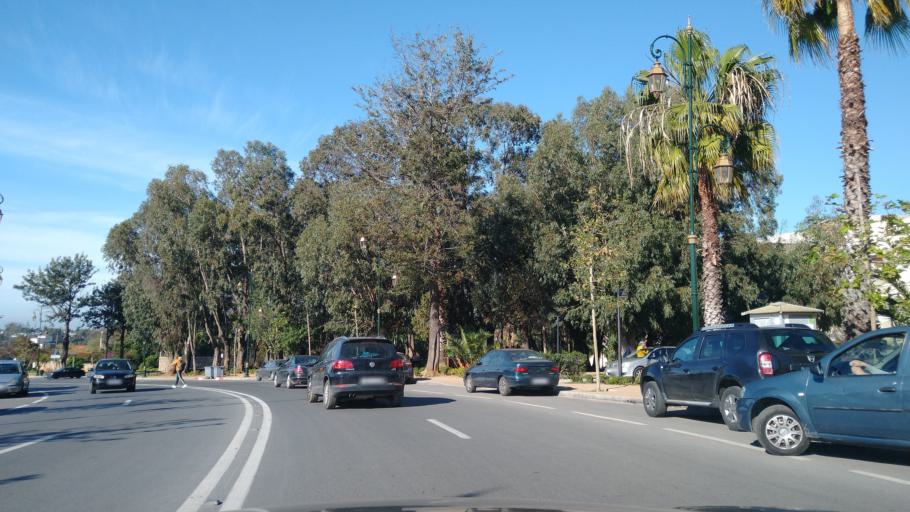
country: MA
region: Rabat-Sale-Zemmour-Zaer
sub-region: Rabat
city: Rabat
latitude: 33.9976
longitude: -6.8192
